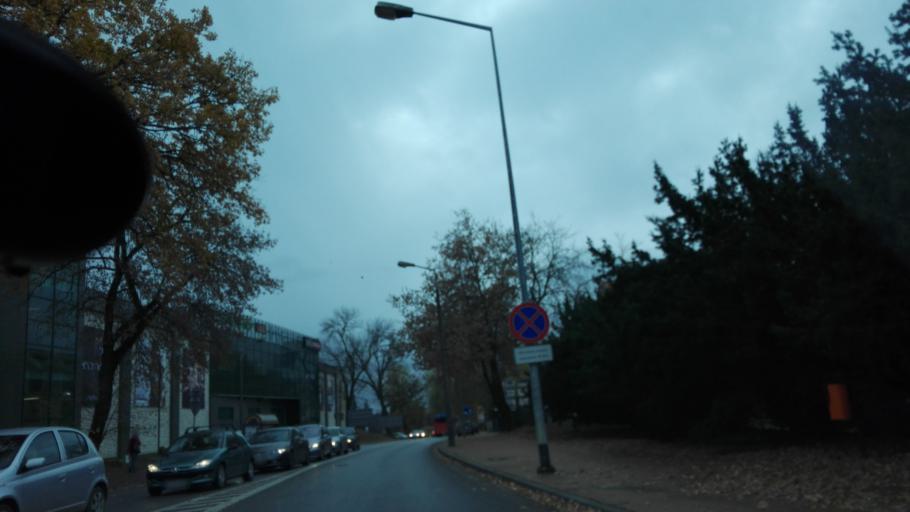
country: PL
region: Lublin Voivodeship
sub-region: Powiat pulawski
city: Pulawy
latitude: 51.4162
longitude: 21.9692
